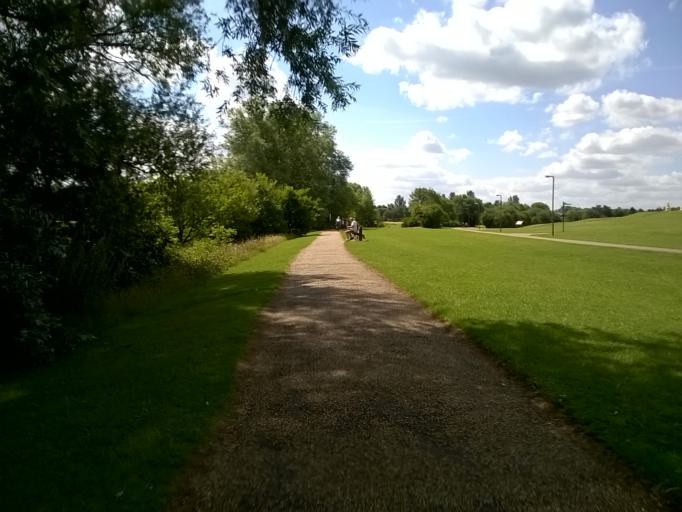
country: GB
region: England
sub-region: Milton Keynes
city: Newport Pagnell
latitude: 52.0586
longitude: -0.7231
